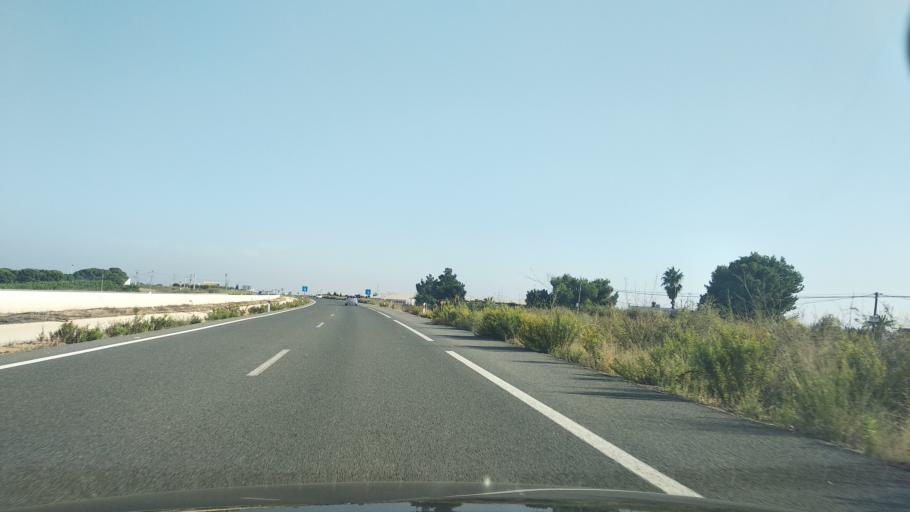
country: ES
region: Murcia
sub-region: Murcia
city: San Javier
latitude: 37.8576
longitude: -0.8877
